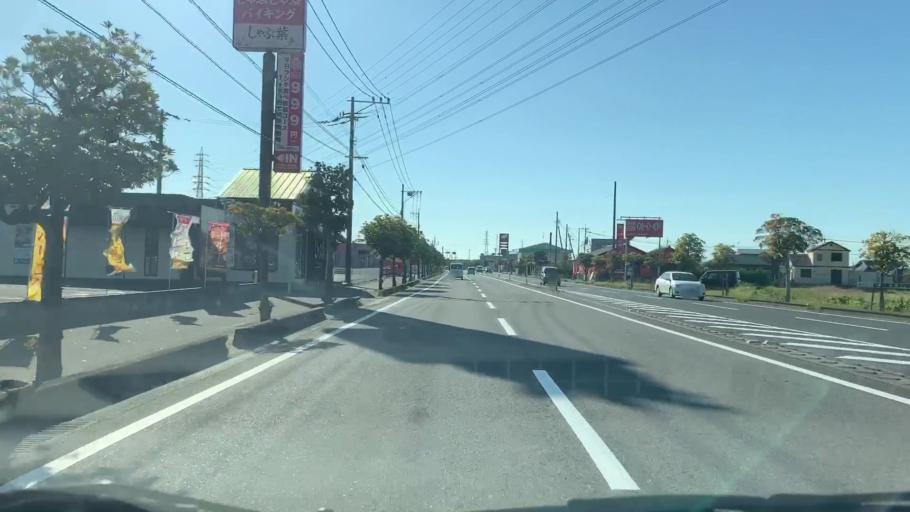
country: JP
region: Saga Prefecture
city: Saga-shi
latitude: 33.3011
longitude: 130.2800
